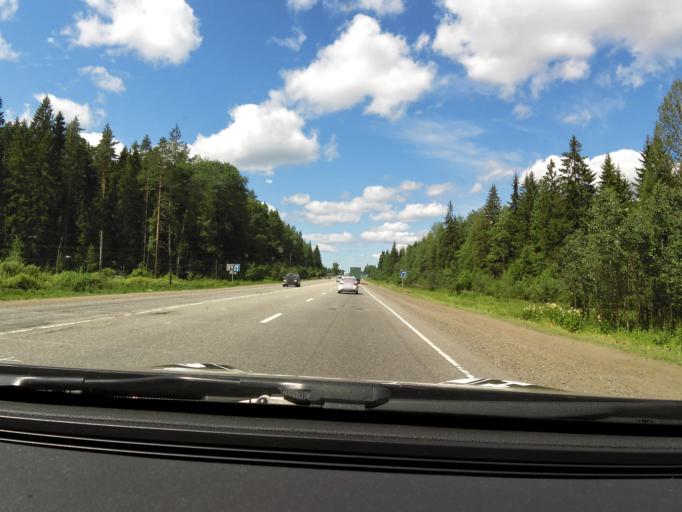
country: RU
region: Tverskaya
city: Kuzhenkino
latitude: 57.7428
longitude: 34.0132
